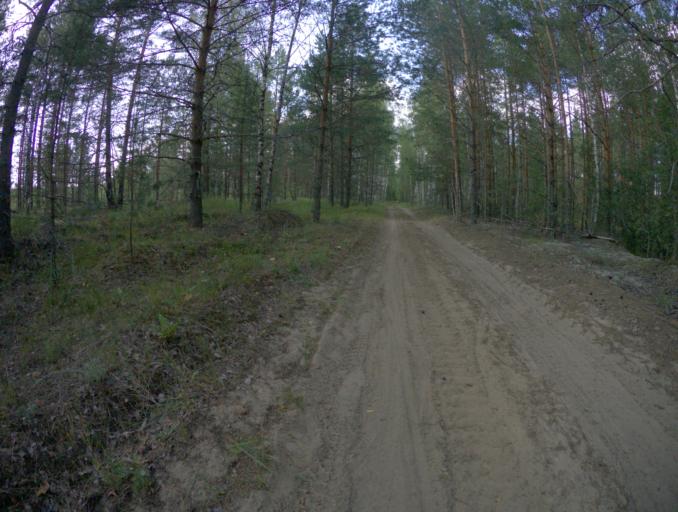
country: RU
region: Vladimir
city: Sobinka
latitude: 55.9336
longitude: 40.0617
